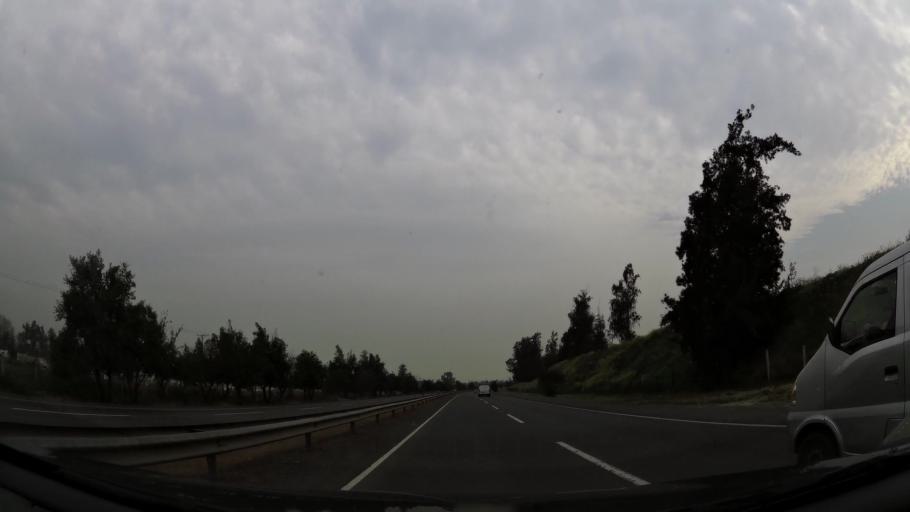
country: CL
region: Santiago Metropolitan
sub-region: Provincia de Chacabuco
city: Chicureo Abajo
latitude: -33.2271
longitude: -70.6845
